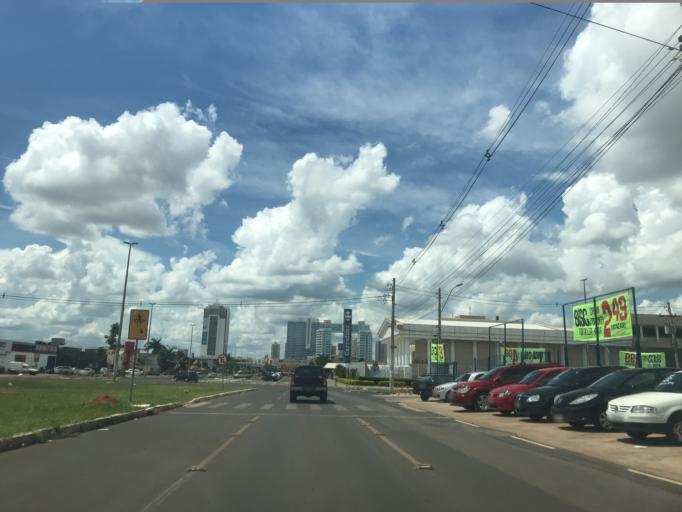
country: BR
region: Federal District
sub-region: Brasilia
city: Brasilia
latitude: -15.8486
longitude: -48.0410
